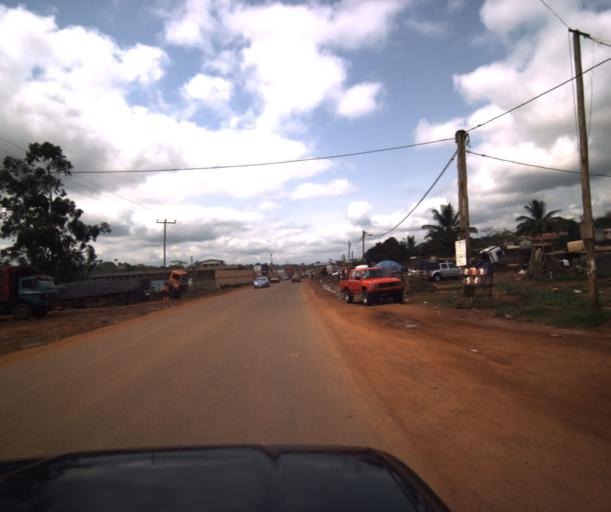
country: CM
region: Centre
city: Yaounde
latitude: 3.8046
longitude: 11.5087
